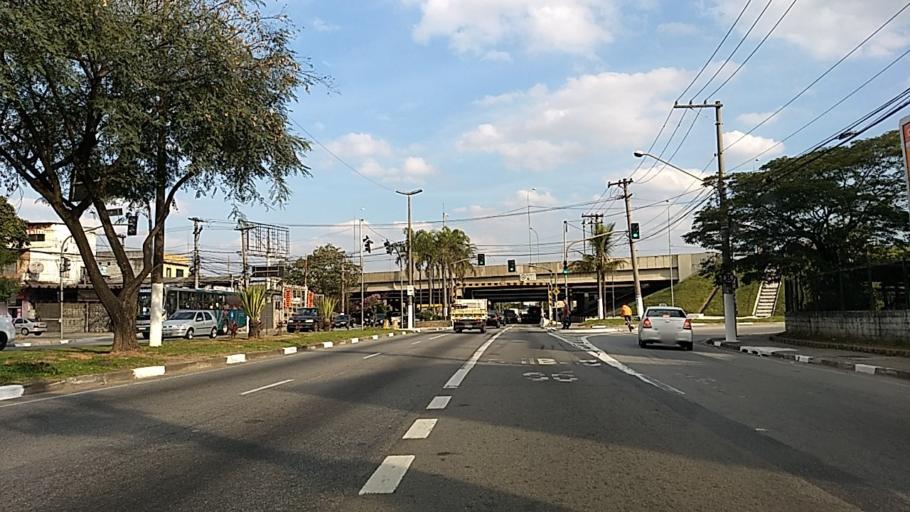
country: BR
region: Sao Paulo
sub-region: Osasco
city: Osasco
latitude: -23.5162
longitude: -46.7885
